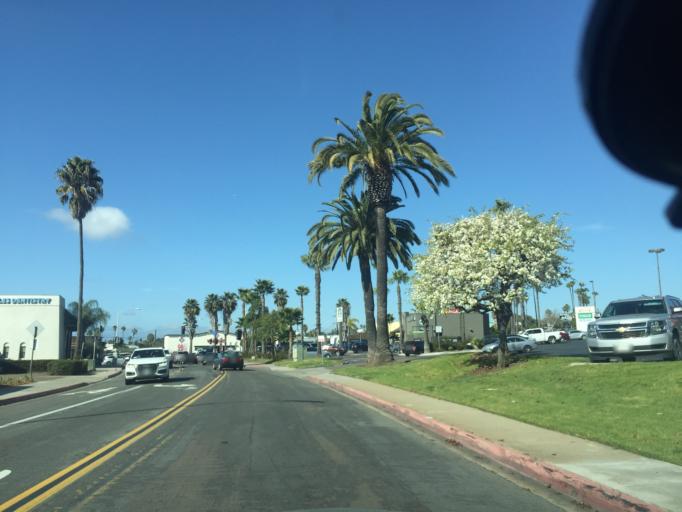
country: US
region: California
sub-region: San Diego County
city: San Diego
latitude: 32.7935
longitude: -117.1936
